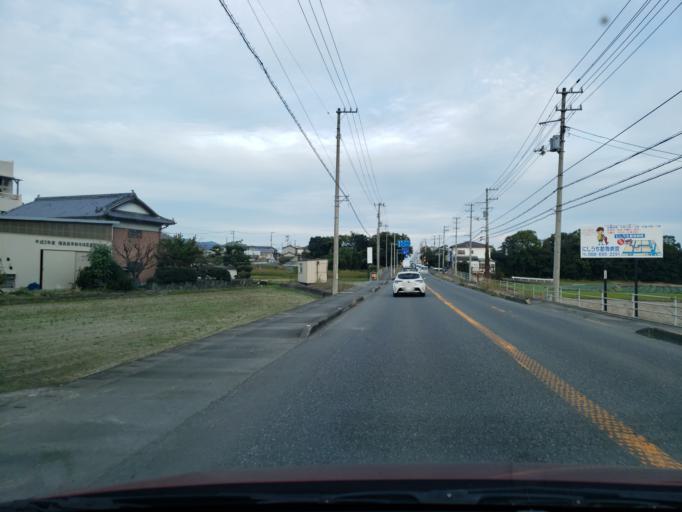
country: JP
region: Tokushima
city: Kamojimacho-jogejima
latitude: 34.0854
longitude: 134.2871
